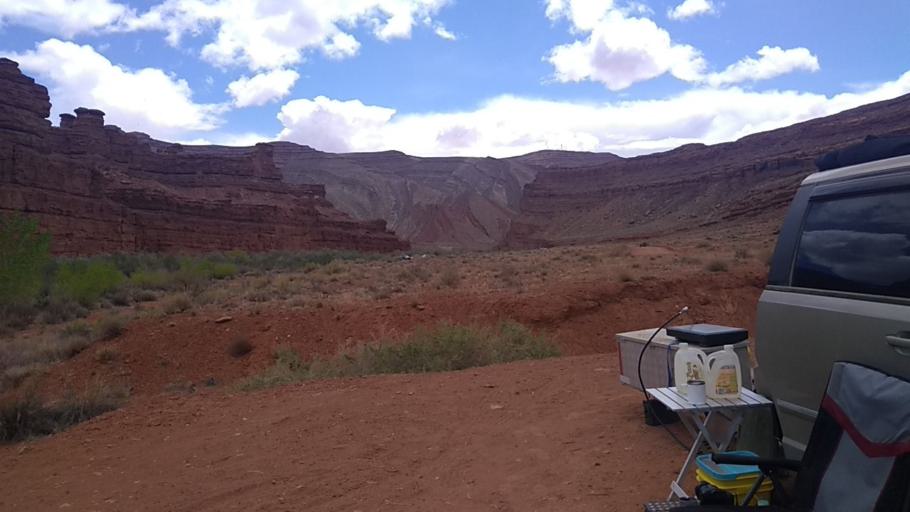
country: US
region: Utah
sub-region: San Juan County
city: Blanding
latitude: 37.1746
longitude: -109.8424
